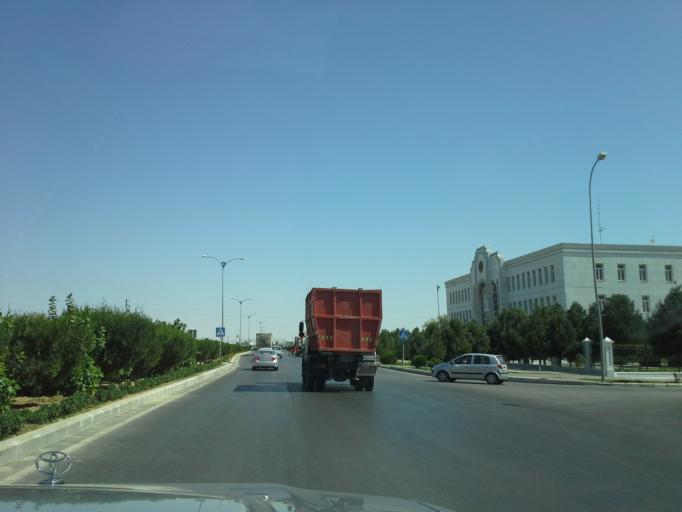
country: TM
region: Ahal
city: Annau
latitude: 37.9106
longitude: 58.4995
